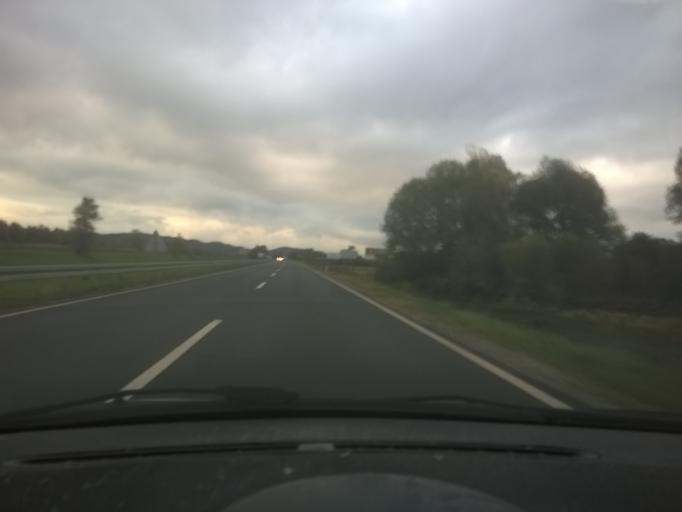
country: HR
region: Zagrebacka
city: Jakovlje
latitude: 45.9946
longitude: 15.8566
